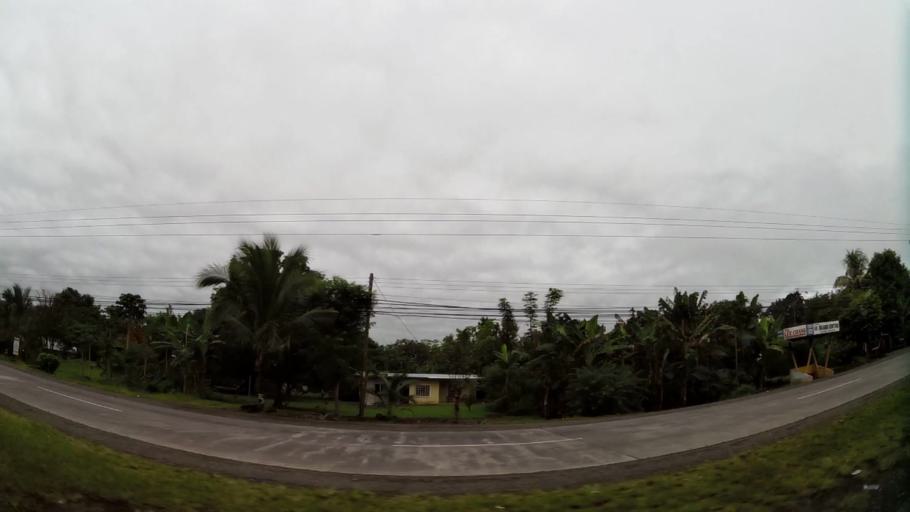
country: PA
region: Chiriqui
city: Boqueron
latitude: 8.4925
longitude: -82.5810
